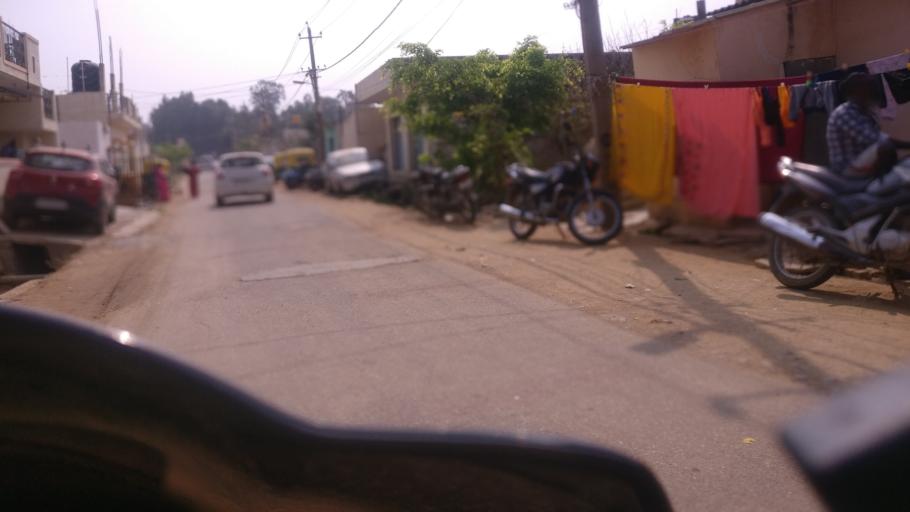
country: IN
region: Karnataka
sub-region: Bangalore Urban
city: Bangalore
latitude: 12.8976
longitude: 77.6822
